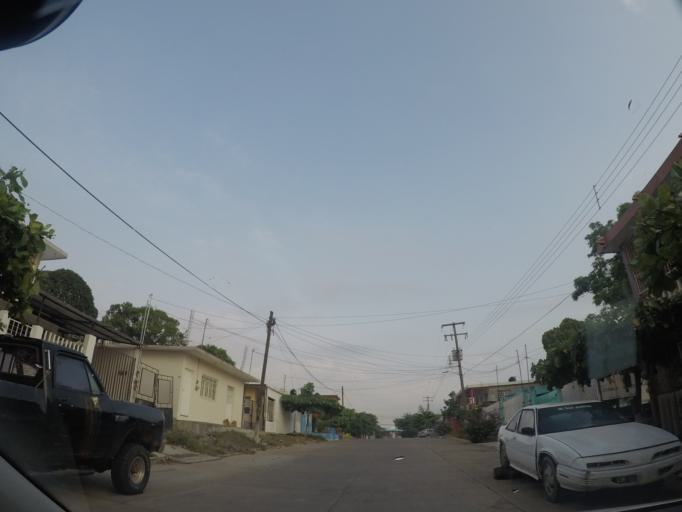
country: MX
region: Oaxaca
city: Matias Romero
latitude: 16.8730
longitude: -95.0405
